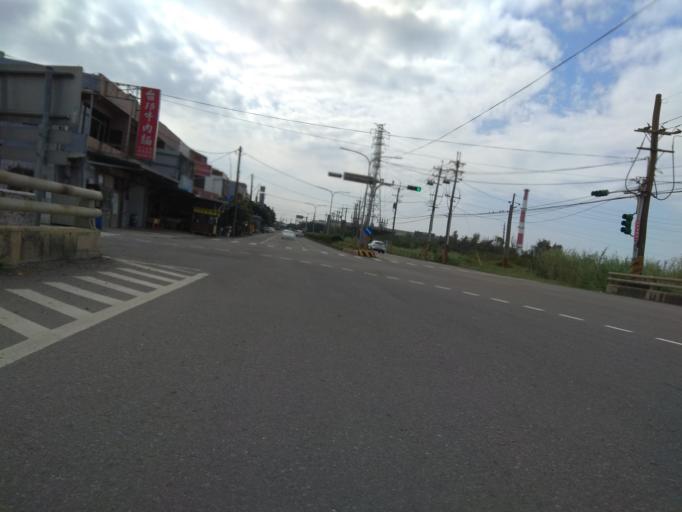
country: TW
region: Taiwan
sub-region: Hsinchu
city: Zhubei
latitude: 24.9864
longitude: 121.0277
